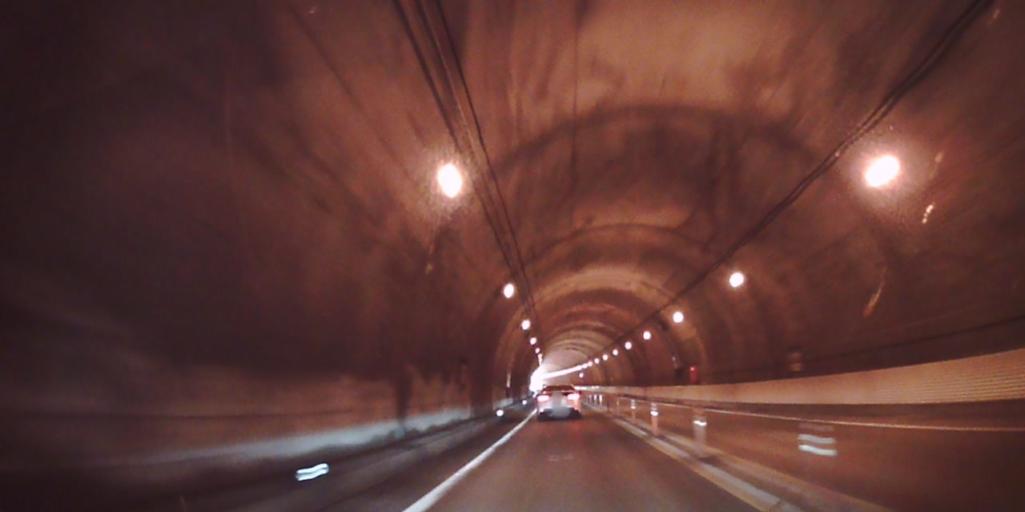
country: JP
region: Hokkaido
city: Date
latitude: 42.5560
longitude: 140.7804
